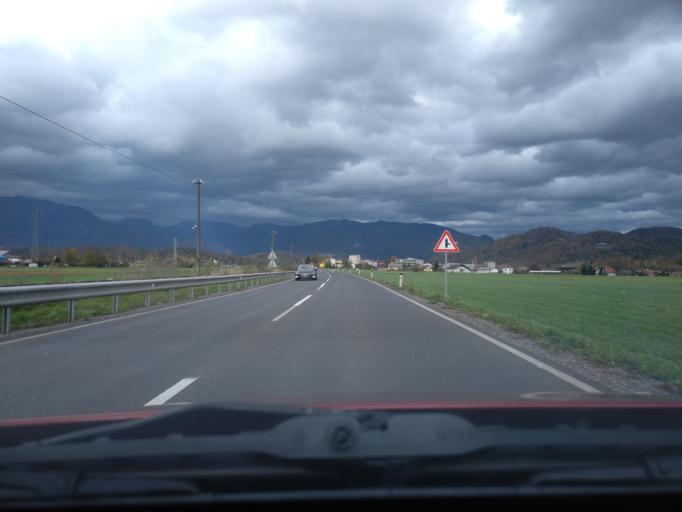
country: SI
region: Kamnik
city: Smarca
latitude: 46.1944
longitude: 14.5896
